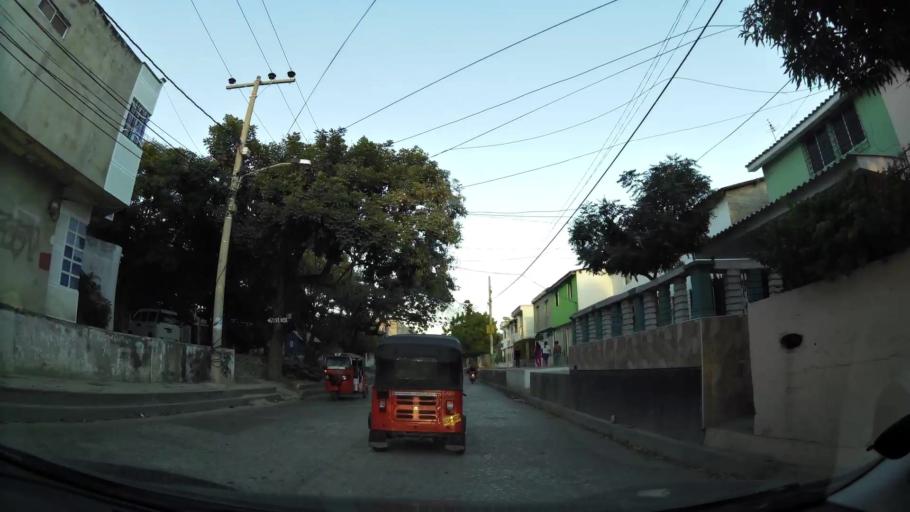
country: CO
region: Atlantico
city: Soledad
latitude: 10.9252
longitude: -74.7829
